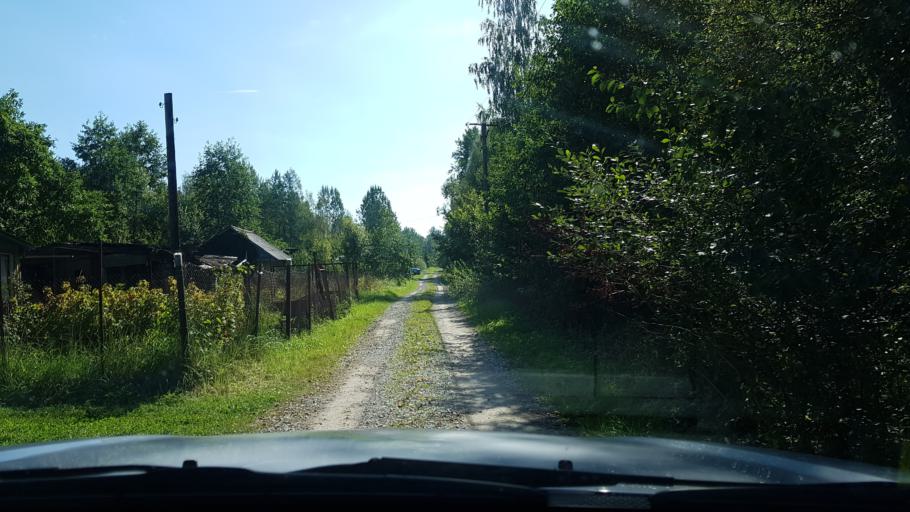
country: EE
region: Ida-Virumaa
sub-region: Sillamaee linn
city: Sillamae
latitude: 59.3175
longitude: 27.7846
